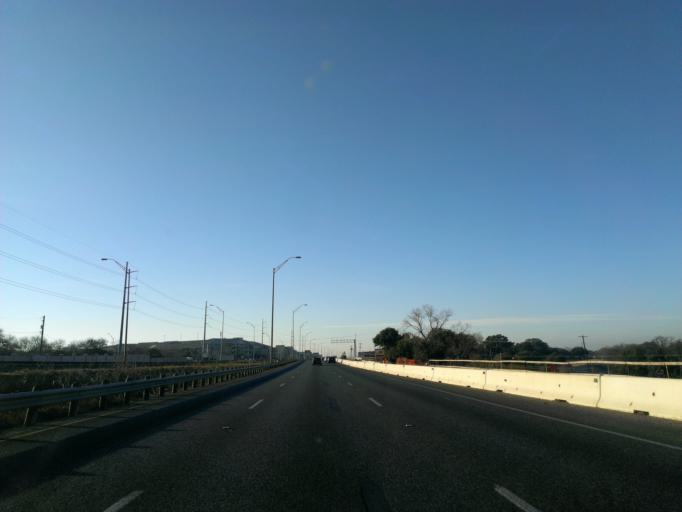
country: US
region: Texas
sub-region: Travis County
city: West Lake Hills
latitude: 30.3237
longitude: -97.7561
